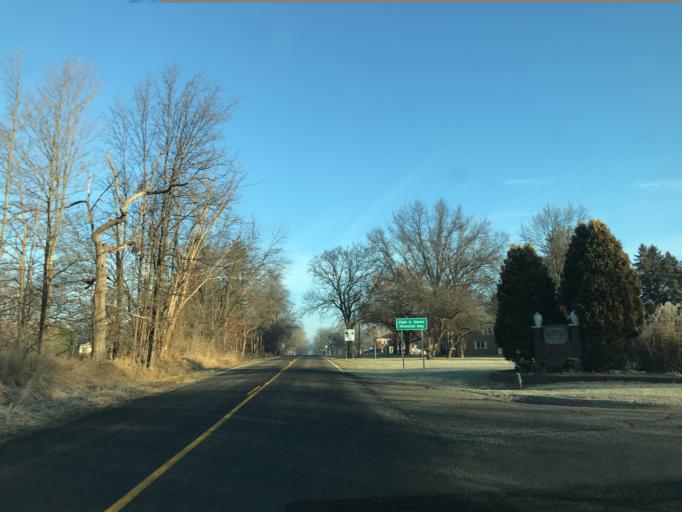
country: US
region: Michigan
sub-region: Eaton County
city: Eaton Rapids
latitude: 42.4725
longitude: -84.6008
